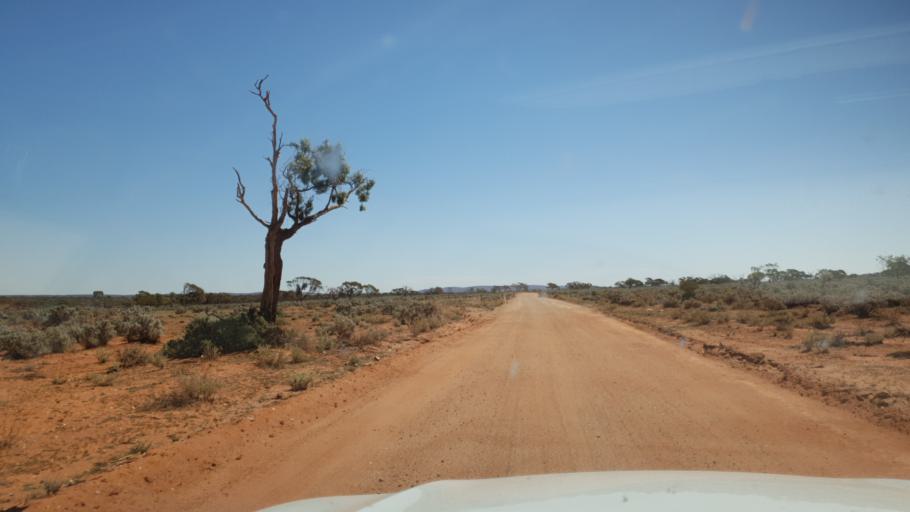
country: AU
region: South Australia
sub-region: Whyalla
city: Whyalla
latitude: -32.6318
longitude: 136.8410
